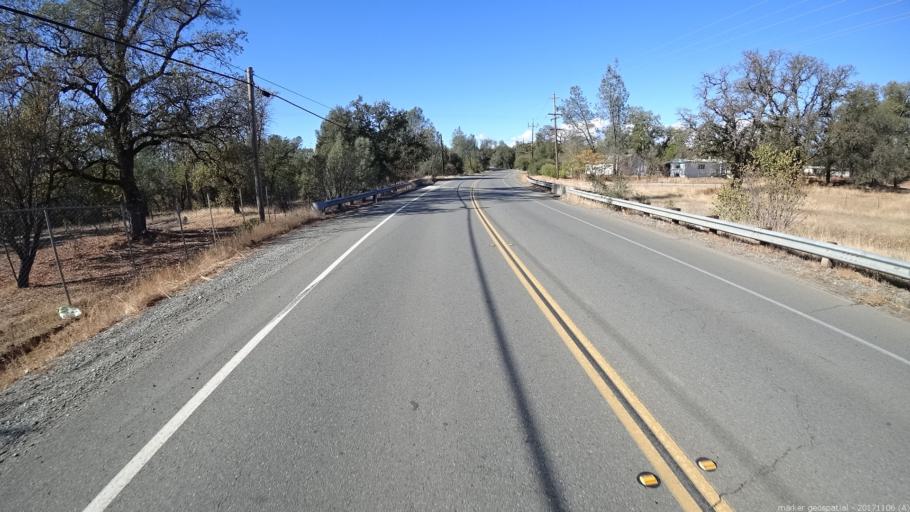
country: US
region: California
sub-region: Shasta County
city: Palo Cedro
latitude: 40.5885
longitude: -122.3019
